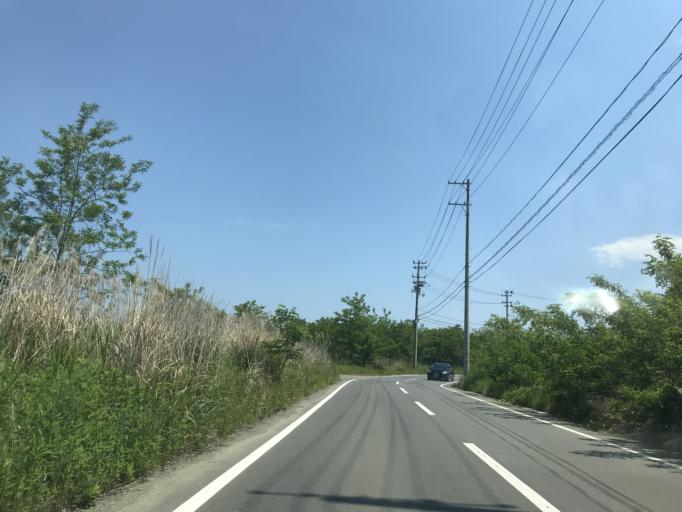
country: JP
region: Miyagi
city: Yamoto
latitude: 38.3697
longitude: 141.1548
